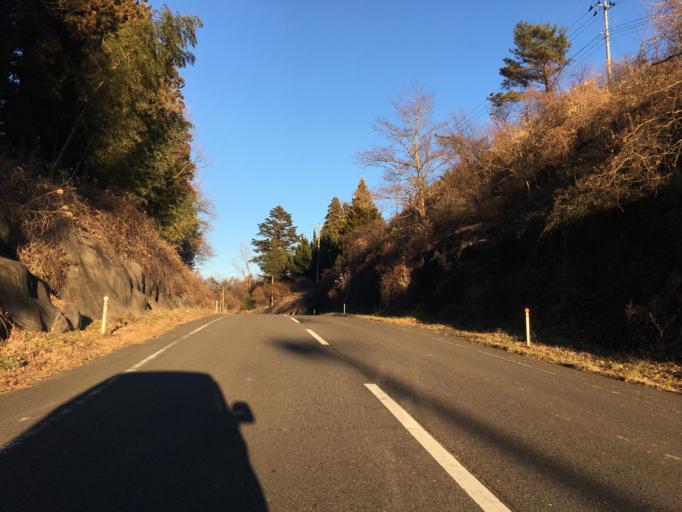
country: JP
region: Fukushima
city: Ishikawa
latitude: 37.1746
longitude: 140.5434
